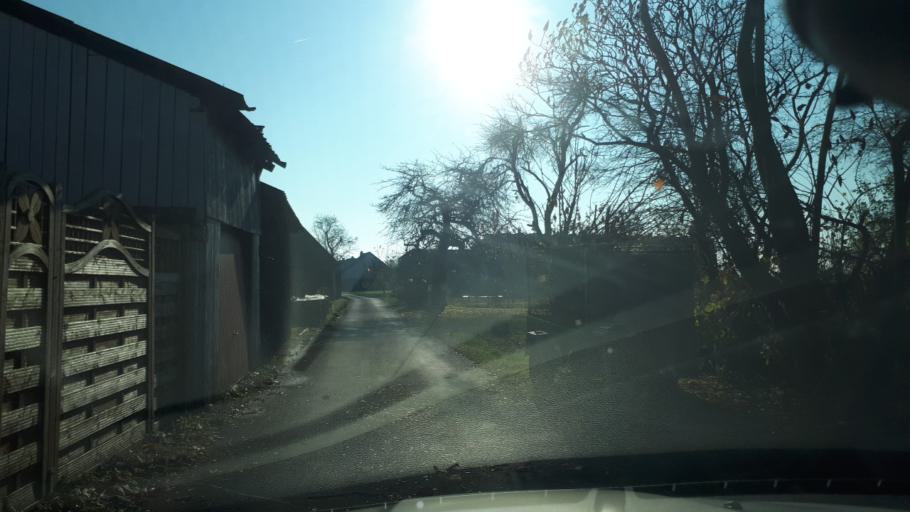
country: DE
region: Rheinland-Pfalz
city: Brieden
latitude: 50.1873
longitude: 7.2628
